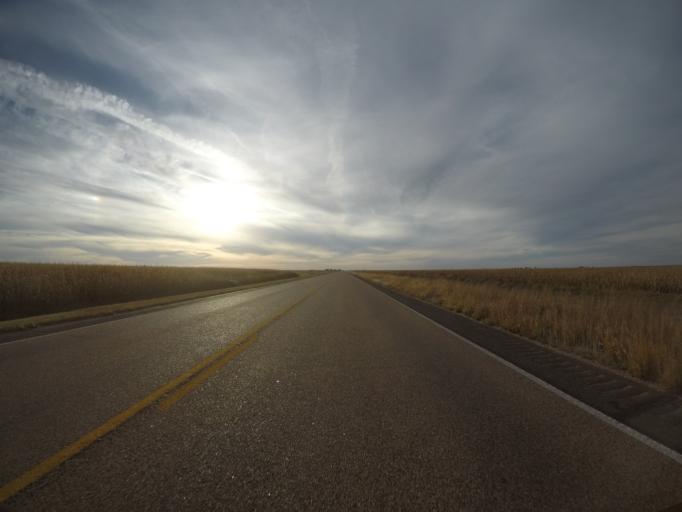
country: US
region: Colorado
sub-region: Kit Carson County
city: Burlington
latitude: 39.6563
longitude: -102.5977
